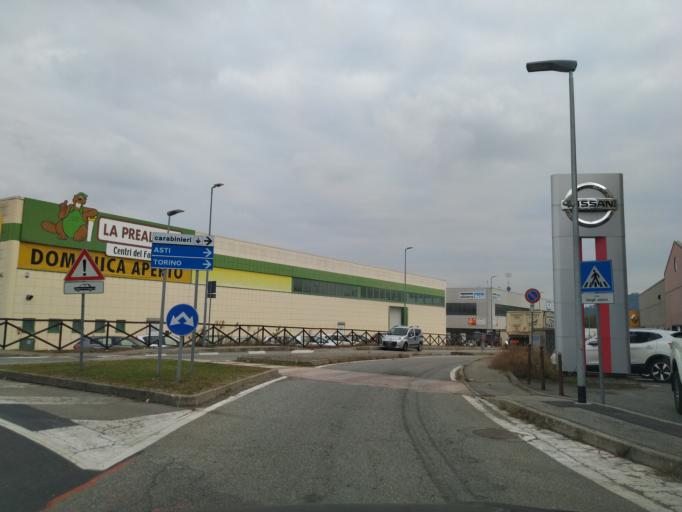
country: IT
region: Piedmont
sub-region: Provincia di Torino
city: Chivasso
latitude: 45.1953
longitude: 7.9166
